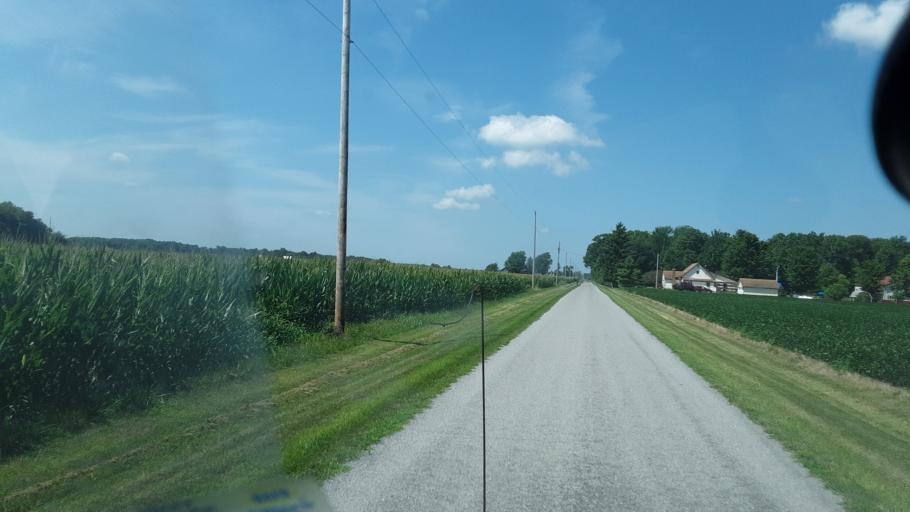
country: US
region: Ohio
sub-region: Hancock County
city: Findlay
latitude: 40.9713
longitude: -83.5602
